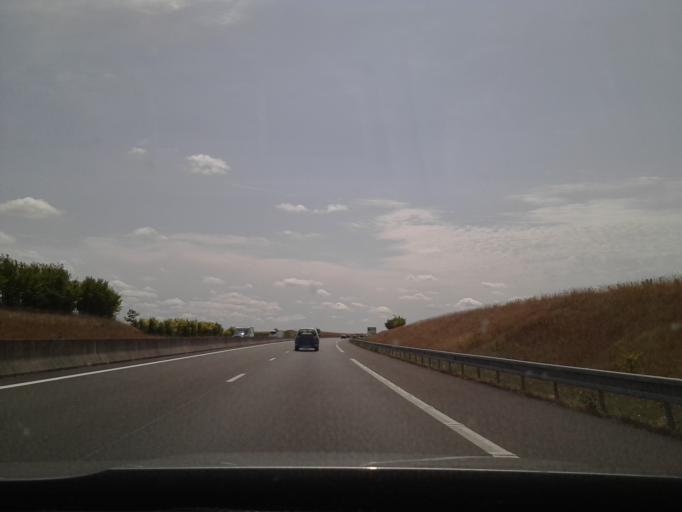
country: FR
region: Centre
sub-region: Departement d'Indre-et-Loire
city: Neuvy-le-Roi
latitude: 47.5773
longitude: 0.5775
